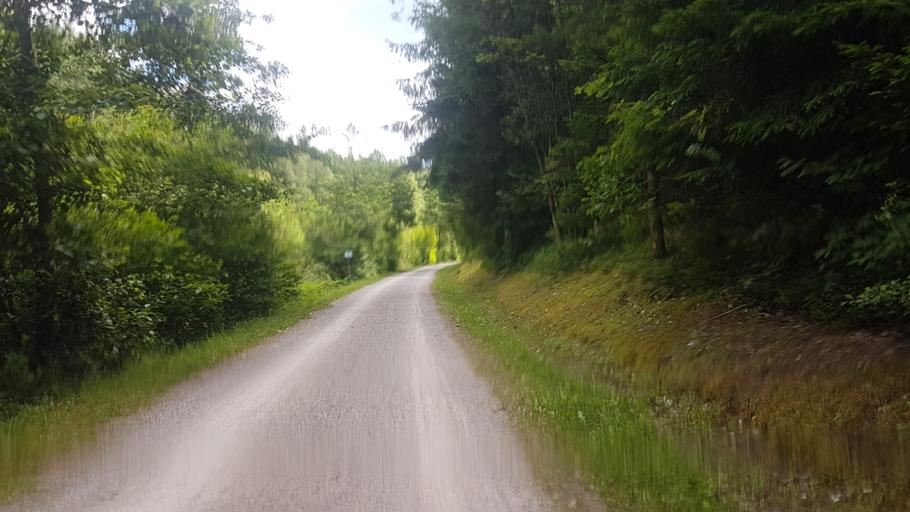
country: DE
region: Bavaria
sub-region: Regierungsbezirk Mittelfranken
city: Pfofeld
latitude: 49.1266
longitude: 10.8337
